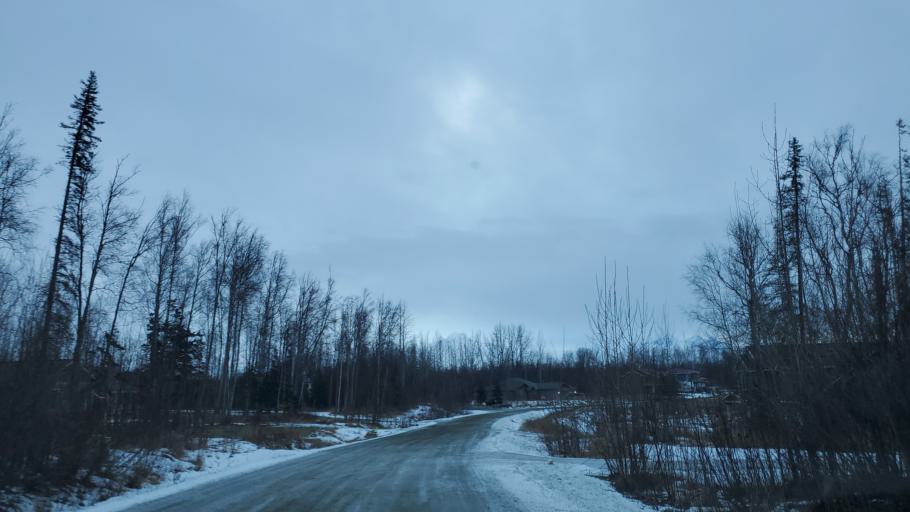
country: US
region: Alaska
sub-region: Matanuska-Susitna Borough
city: Farm Loop
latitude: 61.6560
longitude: -149.2217
